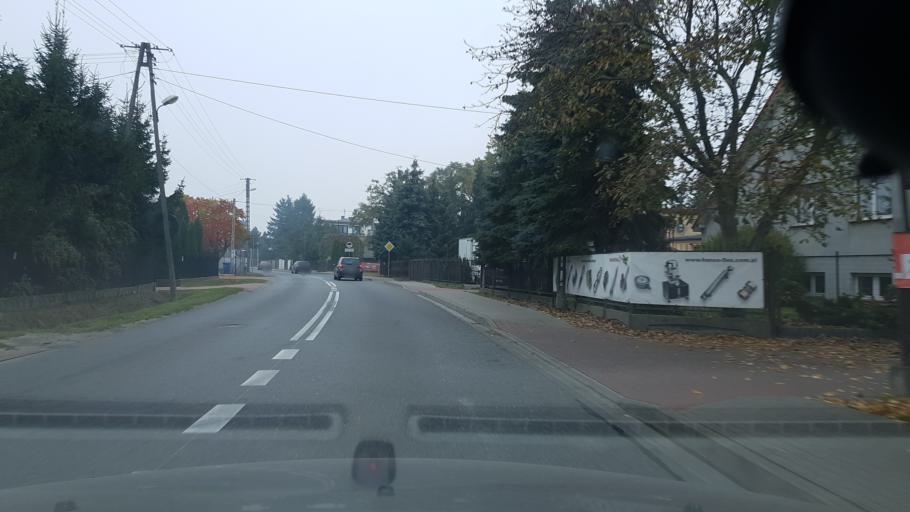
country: PL
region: Masovian Voivodeship
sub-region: Powiat pruszkowski
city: Piastow
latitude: 52.2105
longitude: 20.8394
